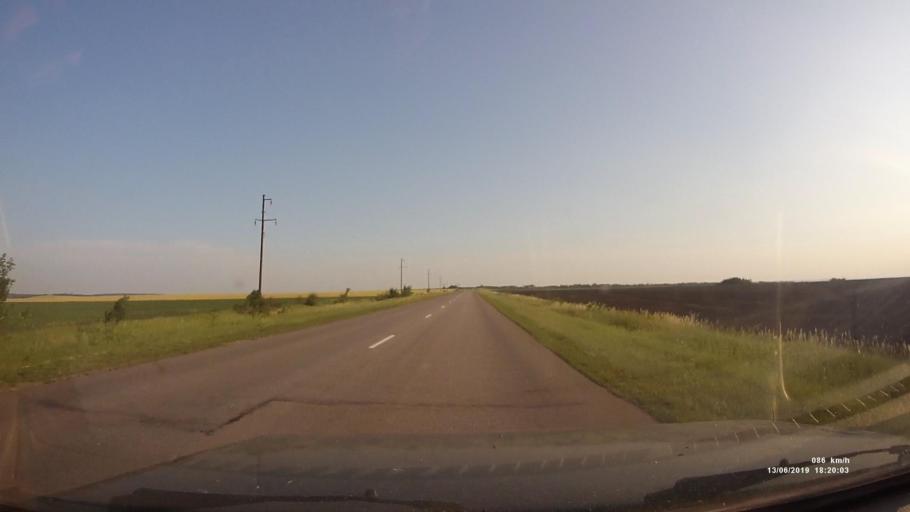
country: RU
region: Rostov
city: Kazanskaya
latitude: 49.8888
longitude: 41.3021
